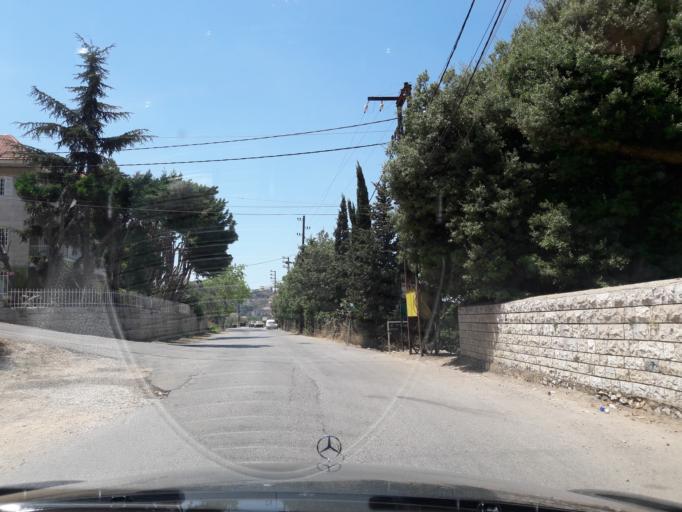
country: LB
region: Mont-Liban
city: Djounie
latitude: 33.9247
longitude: 35.6460
